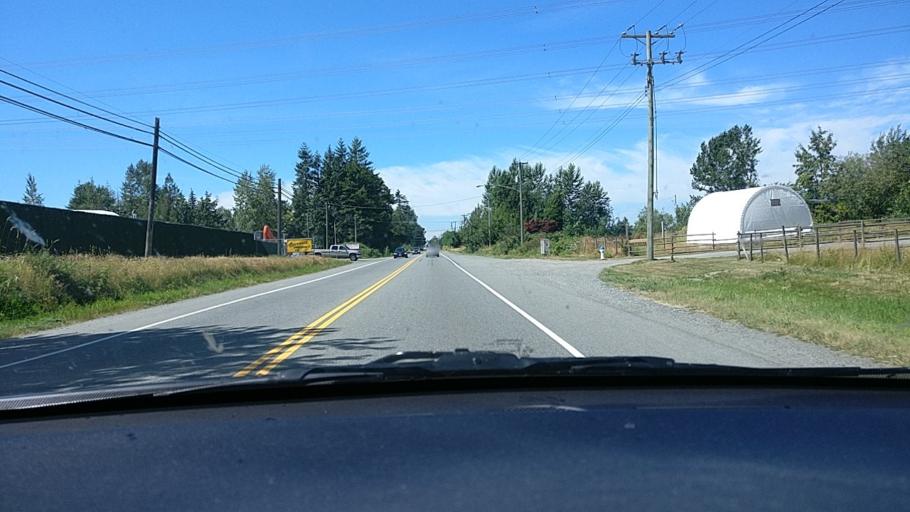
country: CA
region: British Columbia
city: Aldergrove
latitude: 49.0572
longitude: -122.4154
